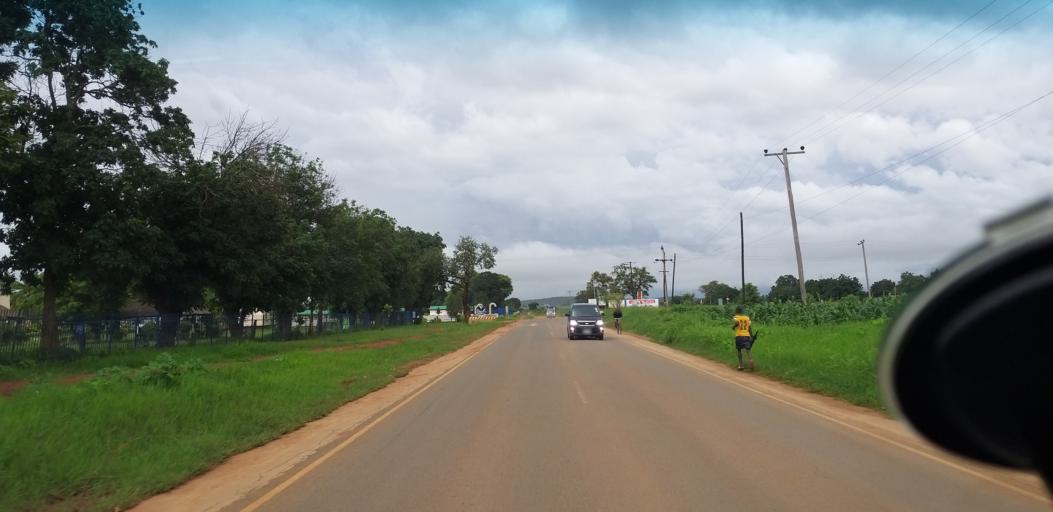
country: ZM
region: Lusaka
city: Lusaka
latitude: -15.5196
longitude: 28.2975
